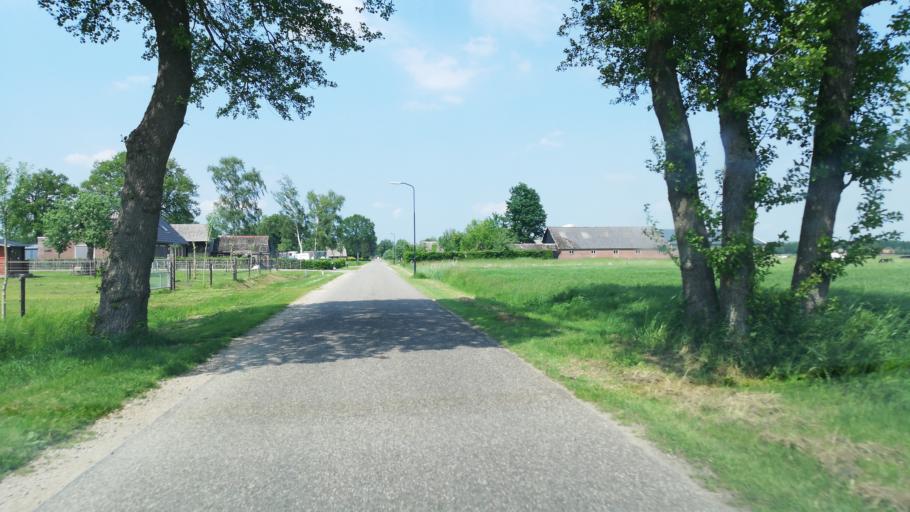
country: NL
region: Gelderland
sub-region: Gemeente Epe
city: Vaassen
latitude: 52.2585
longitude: 5.9897
